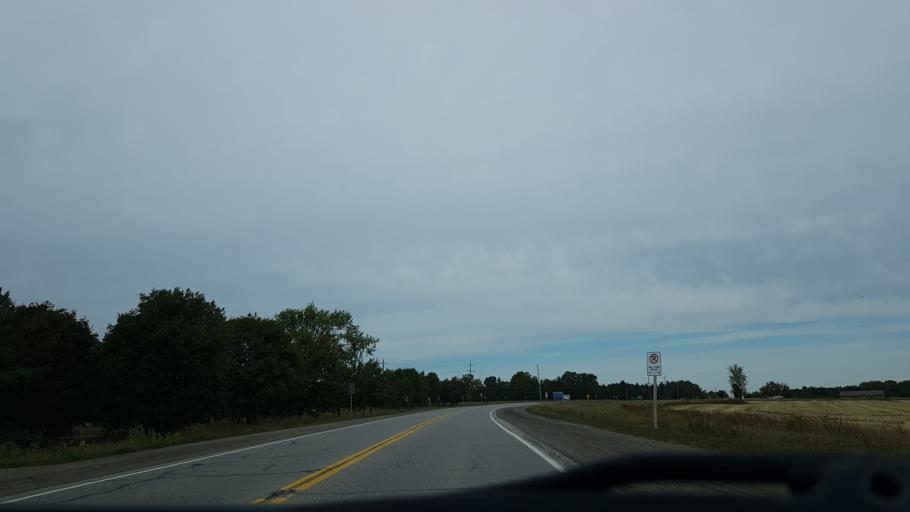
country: CA
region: Ontario
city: Orangeville
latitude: 43.8262
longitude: -80.0346
